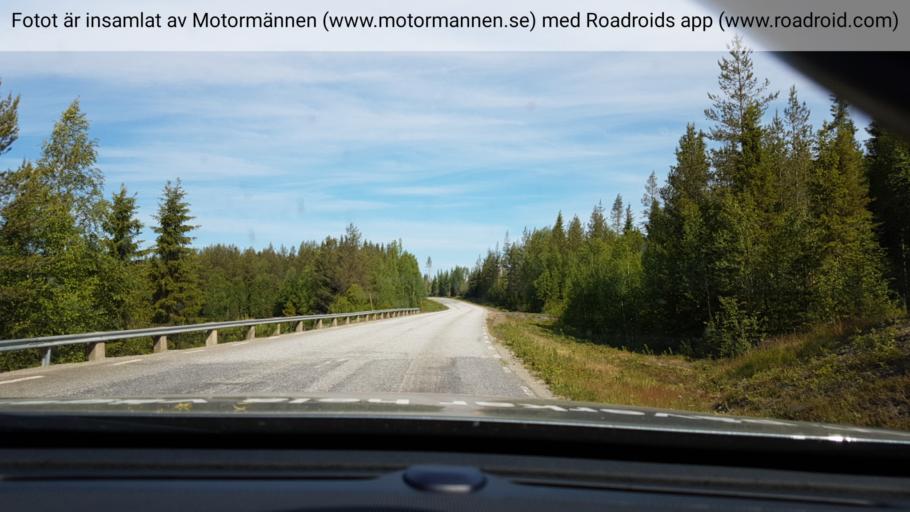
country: SE
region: Vaesterbotten
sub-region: Vilhelmina Kommun
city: Sjoberg
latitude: 64.6058
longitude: 15.8566
